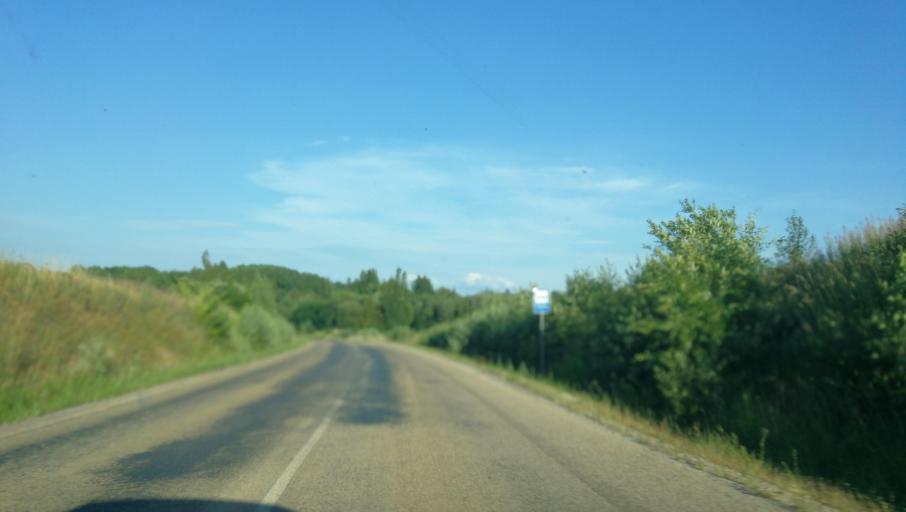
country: LV
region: Priekuli
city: Priekuli
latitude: 57.2601
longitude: 25.3606
